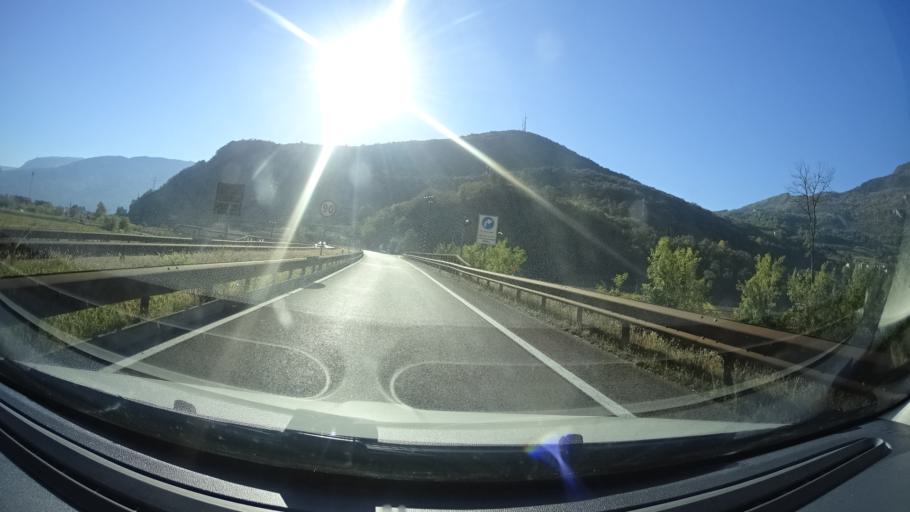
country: IT
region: Trentino-Alto Adige
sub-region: Provincia di Trento
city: Mori
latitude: 45.8530
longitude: 10.9589
